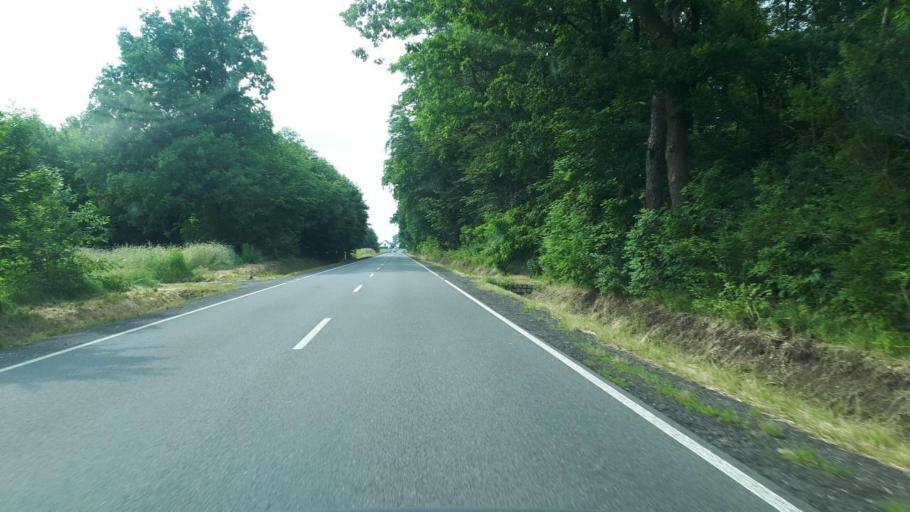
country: PL
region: Silesian Voivodeship
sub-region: Powiat tarnogorski
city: Krupski Mlyn
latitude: 50.5511
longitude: 18.5639
